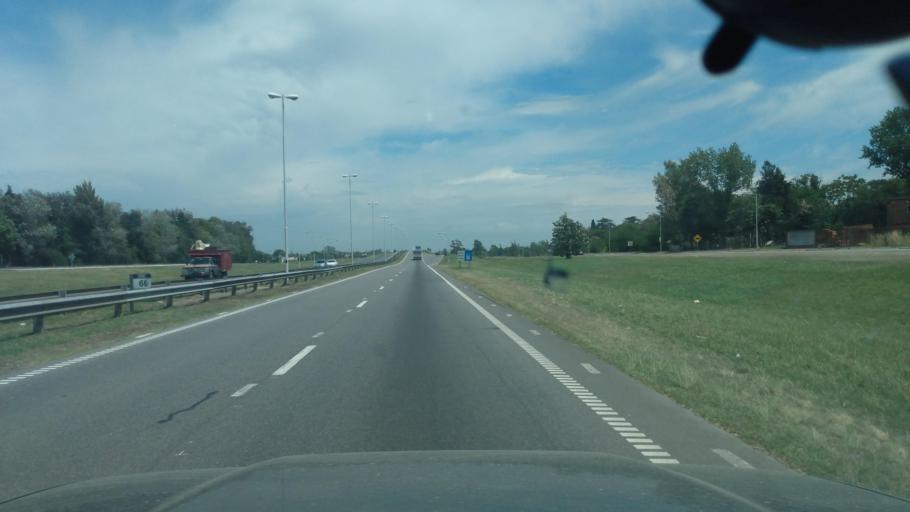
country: AR
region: Buenos Aires
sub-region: Partido de Lujan
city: Lujan
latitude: -34.5583
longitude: -59.0954
